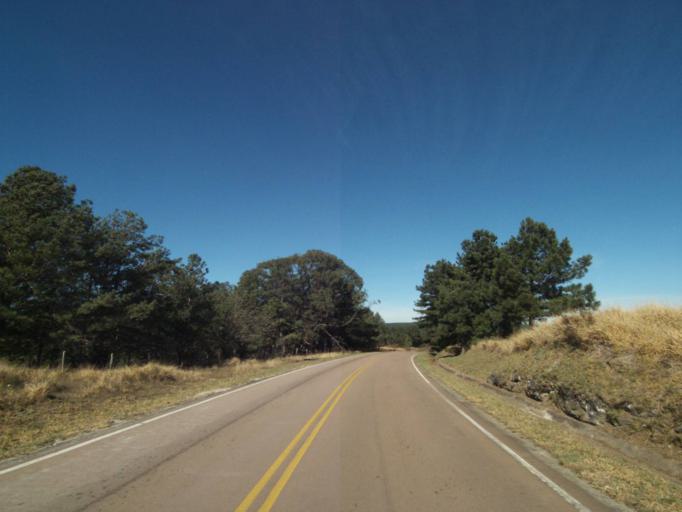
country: BR
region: Parana
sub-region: Tibagi
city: Tibagi
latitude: -24.6068
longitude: -50.2585
